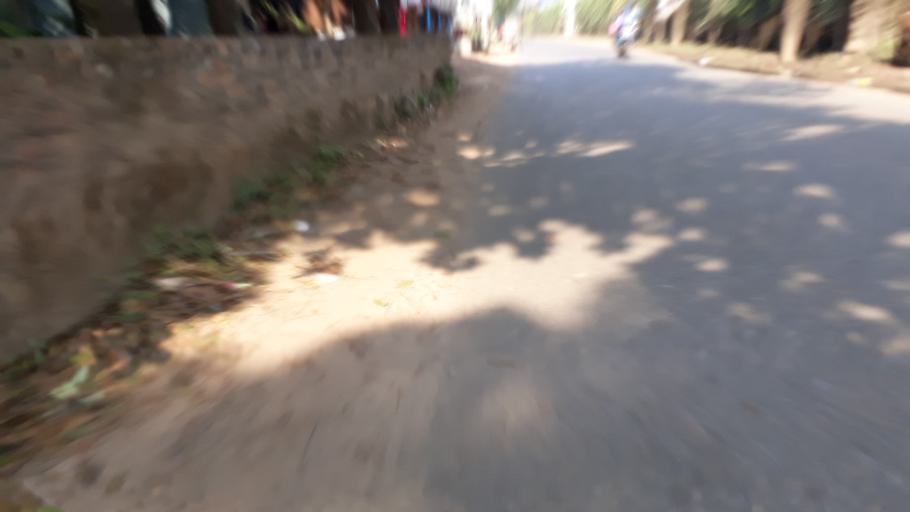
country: BD
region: Dhaka
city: Tungi
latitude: 23.8627
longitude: 90.3109
